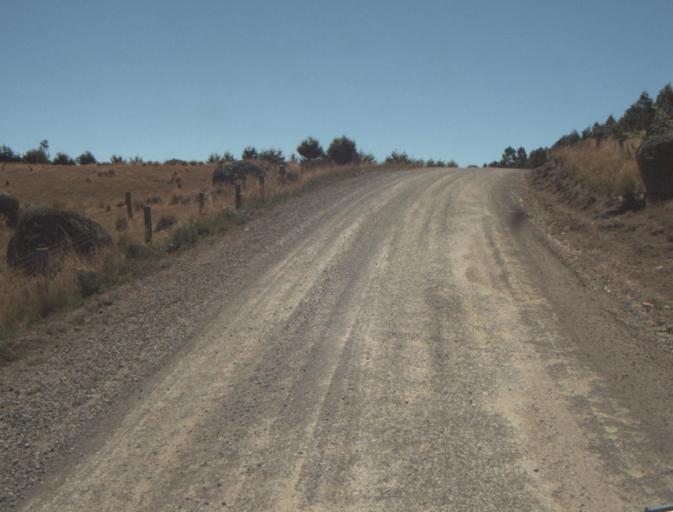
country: AU
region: Tasmania
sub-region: Dorset
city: Scottsdale
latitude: -41.3502
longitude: 147.4497
